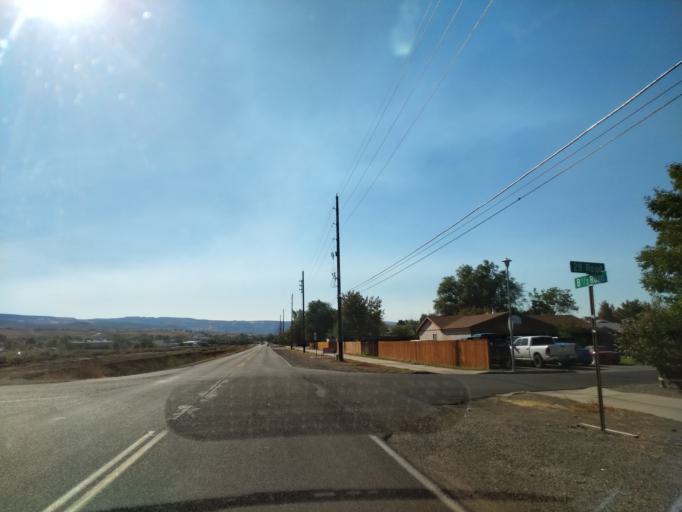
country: US
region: Colorado
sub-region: Mesa County
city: Orchard Mesa
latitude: 39.0411
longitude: -108.5334
